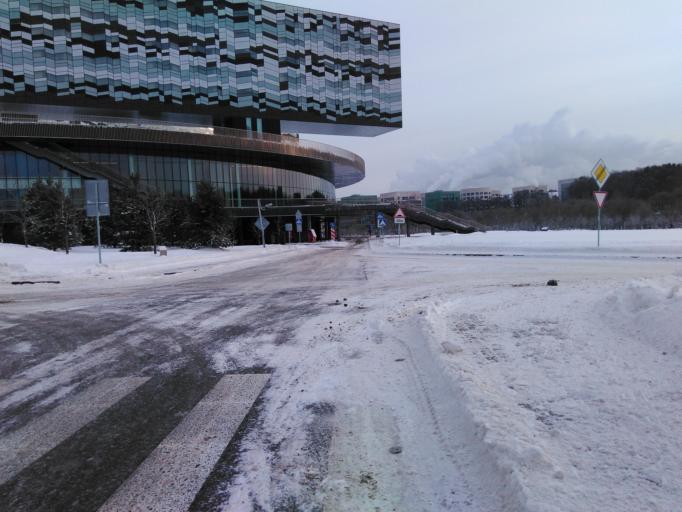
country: RU
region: Moskovskaya
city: Zarech'ye
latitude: 55.6947
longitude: 37.3885
